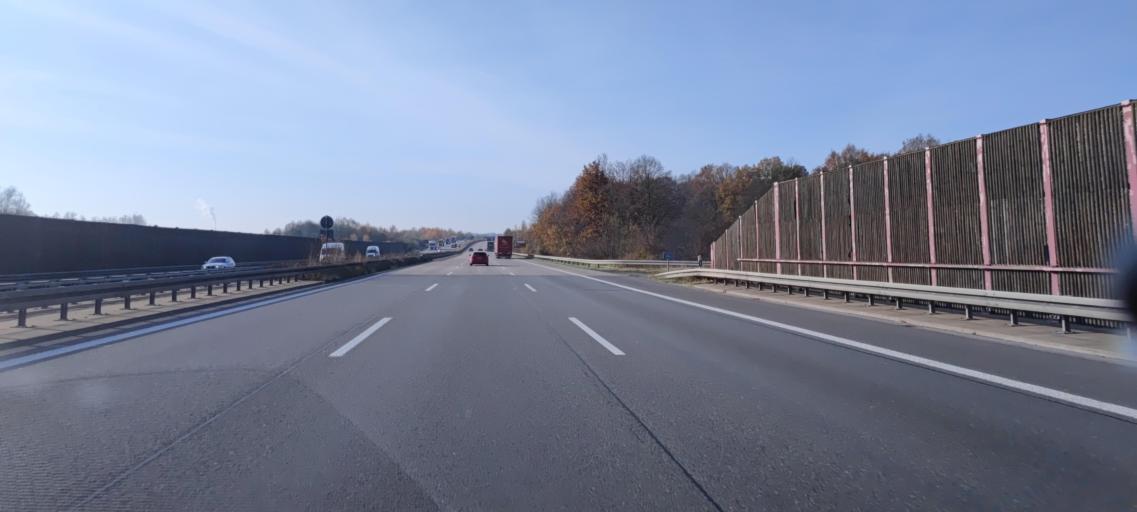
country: DE
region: Saxony
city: Frankenberg
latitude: 50.9180
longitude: 13.0275
